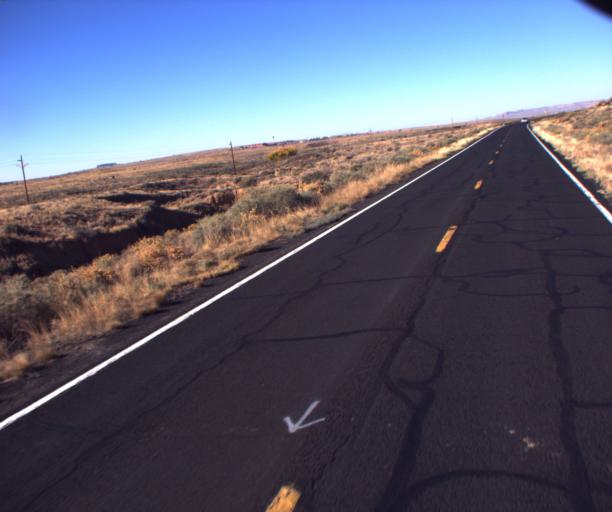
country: US
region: Arizona
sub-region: Navajo County
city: First Mesa
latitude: 35.8299
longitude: -110.2787
